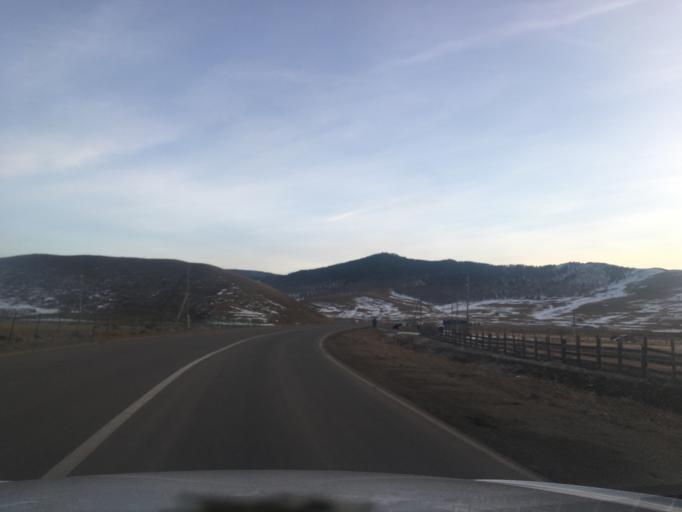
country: MN
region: Ulaanbaatar
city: Ulaanbaatar
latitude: 48.1021
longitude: 106.7368
